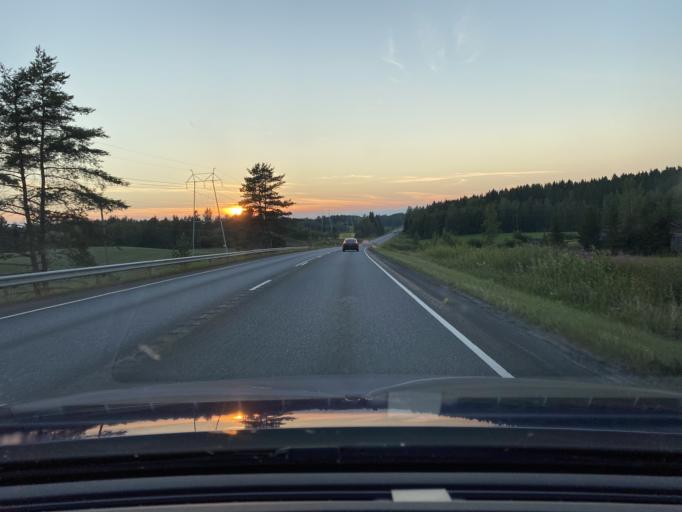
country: FI
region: Pirkanmaa
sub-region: Luoteis-Pirkanmaa
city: Ikaalinen
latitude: 61.8050
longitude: 22.9669
